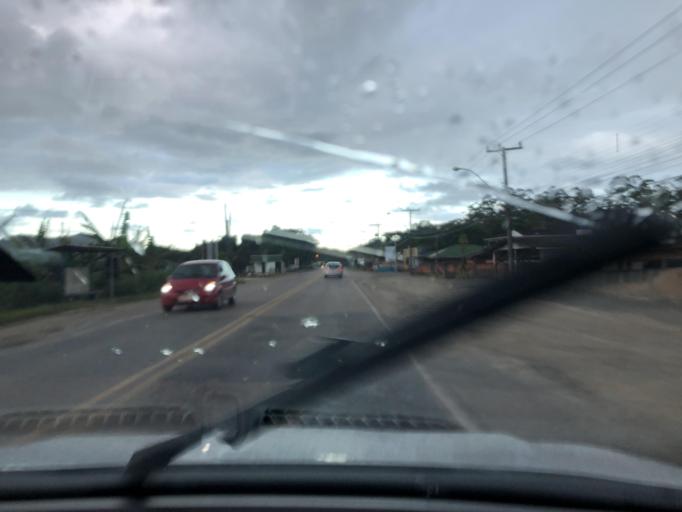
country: BR
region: Santa Catarina
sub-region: Sao Francisco Do Sul
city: Sao Francisco do Sul
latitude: -26.2134
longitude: -48.5594
